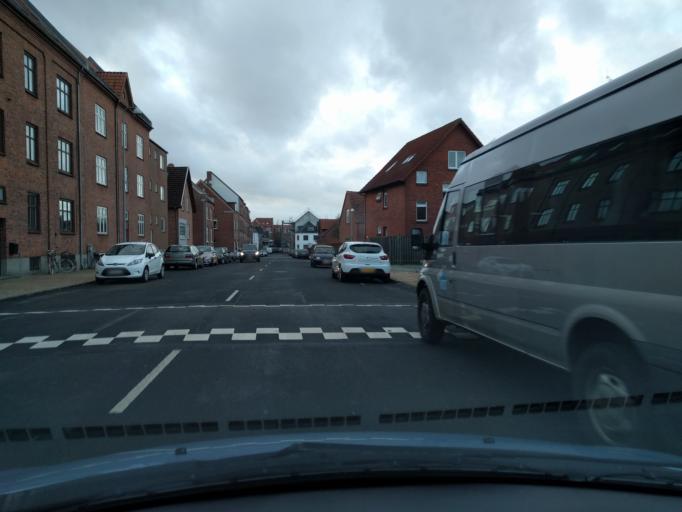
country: DK
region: South Denmark
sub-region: Odense Kommune
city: Odense
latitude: 55.4084
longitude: 10.3974
